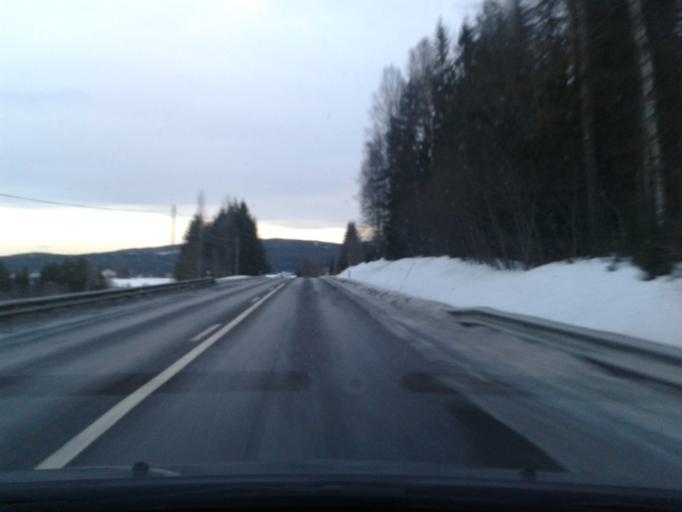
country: SE
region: Vaesternorrland
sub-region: Kramfors Kommun
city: Bollstabruk
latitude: 63.0819
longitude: 17.5376
